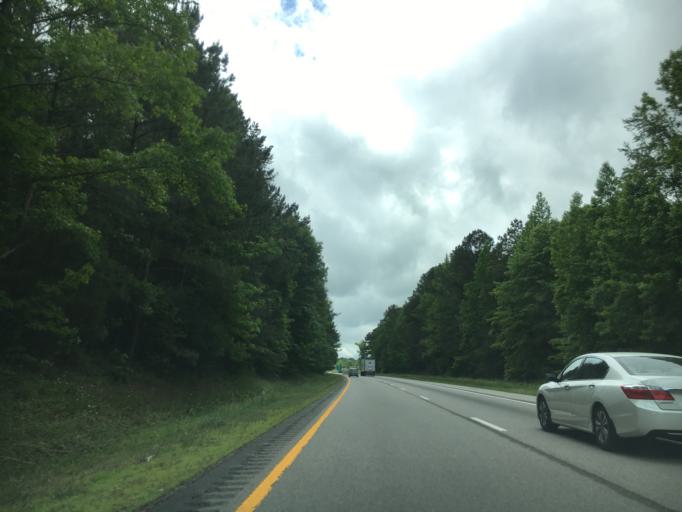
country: US
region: Virginia
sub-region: Mecklenburg County
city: South Hill
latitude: 36.7581
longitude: -78.0880
